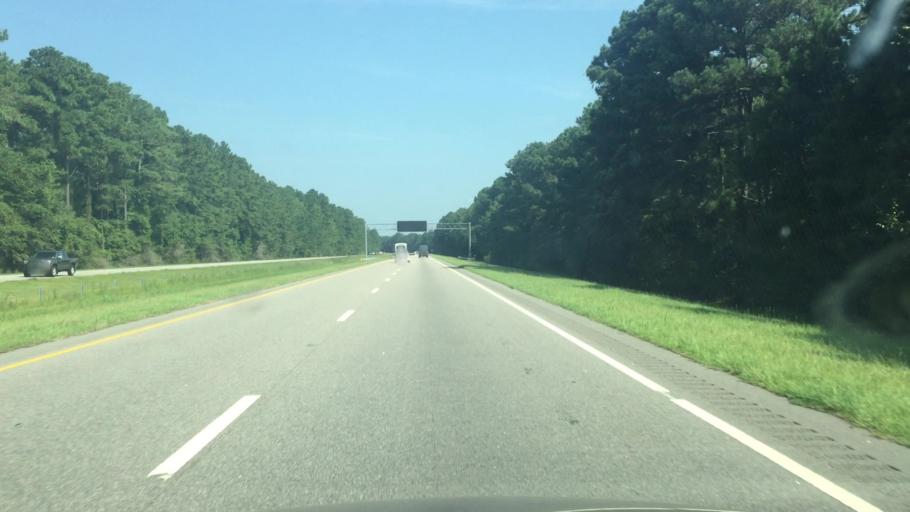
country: US
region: North Carolina
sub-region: Robeson County
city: Lumberton
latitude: 34.5565
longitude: -79.0254
